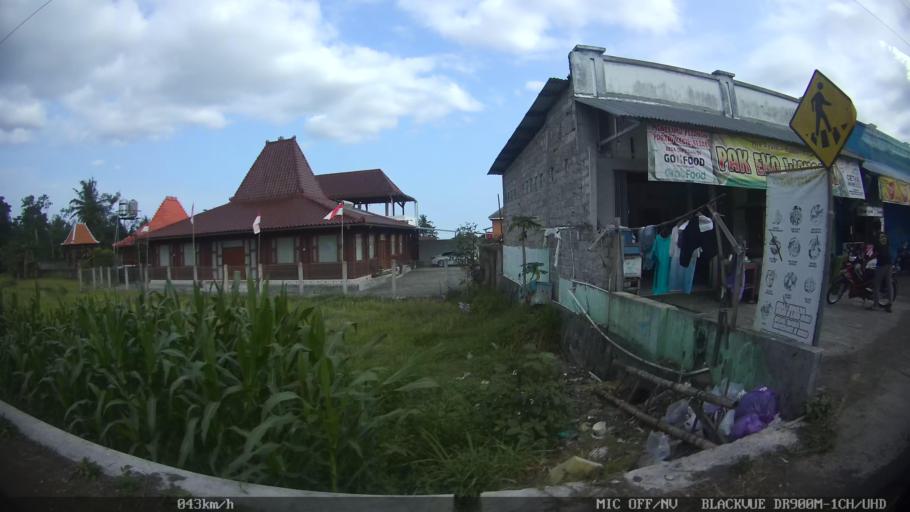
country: ID
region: Daerah Istimewa Yogyakarta
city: Depok
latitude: -7.6824
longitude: 110.4411
